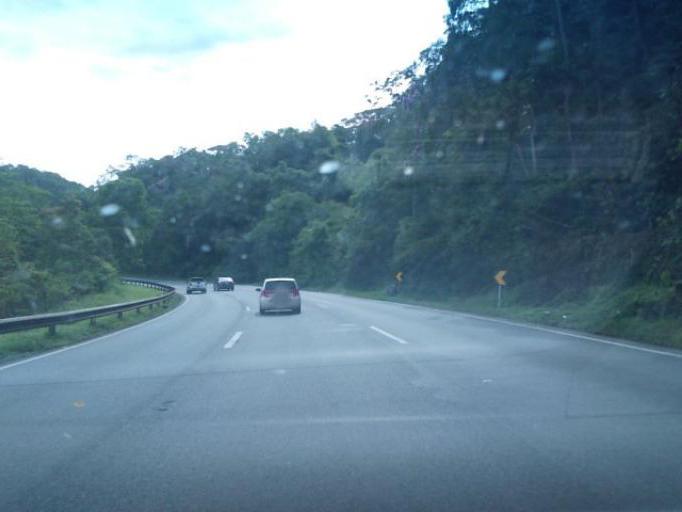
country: BR
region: Sao Paulo
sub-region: Cajati
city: Cajati
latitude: -24.8940
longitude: -48.2438
